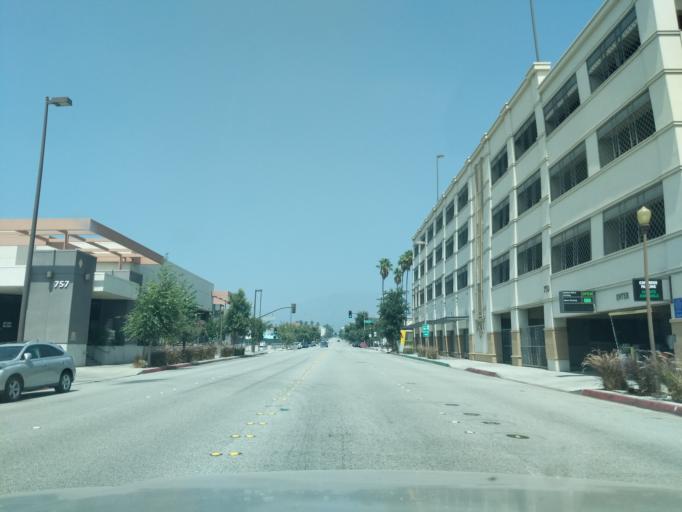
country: US
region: California
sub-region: Los Angeles County
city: South Pasadena
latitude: 34.1321
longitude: -118.1488
